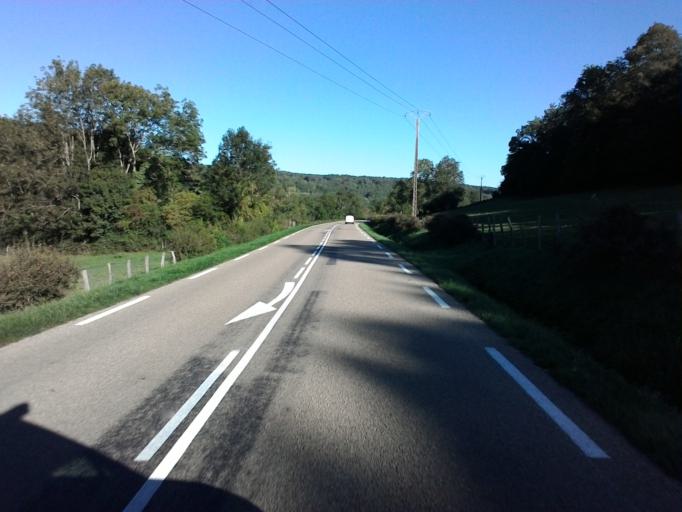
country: FR
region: Bourgogne
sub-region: Departement de la Cote-d'Or
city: Montbard
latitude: 47.6045
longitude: 4.3198
